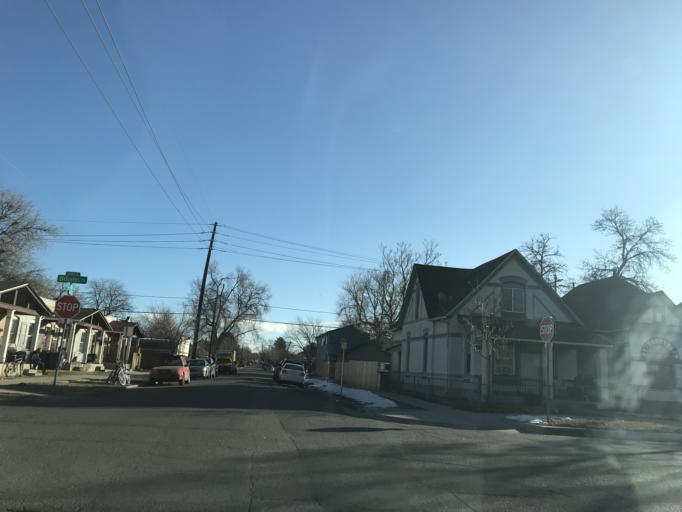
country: US
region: Colorado
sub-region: Denver County
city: Denver
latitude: 39.7682
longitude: -104.9661
